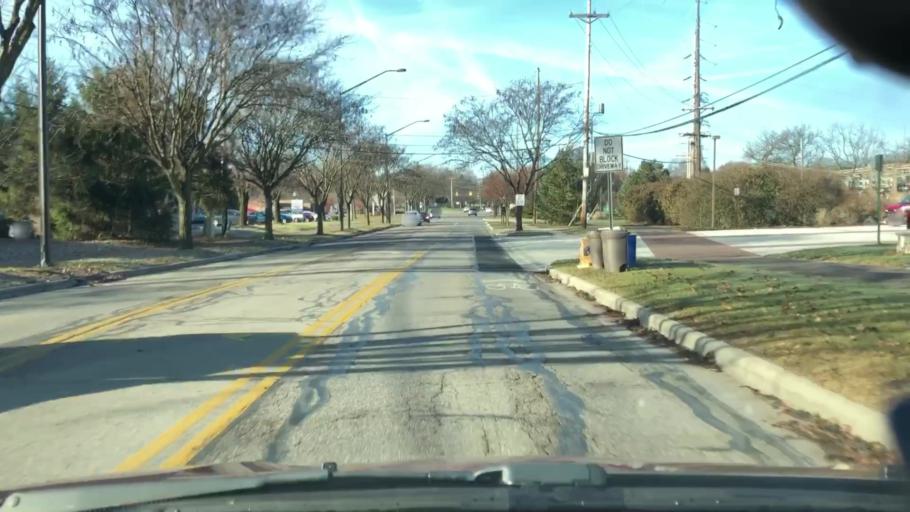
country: US
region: Ohio
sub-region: Franklin County
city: Westerville
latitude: 40.1251
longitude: -82.9449
